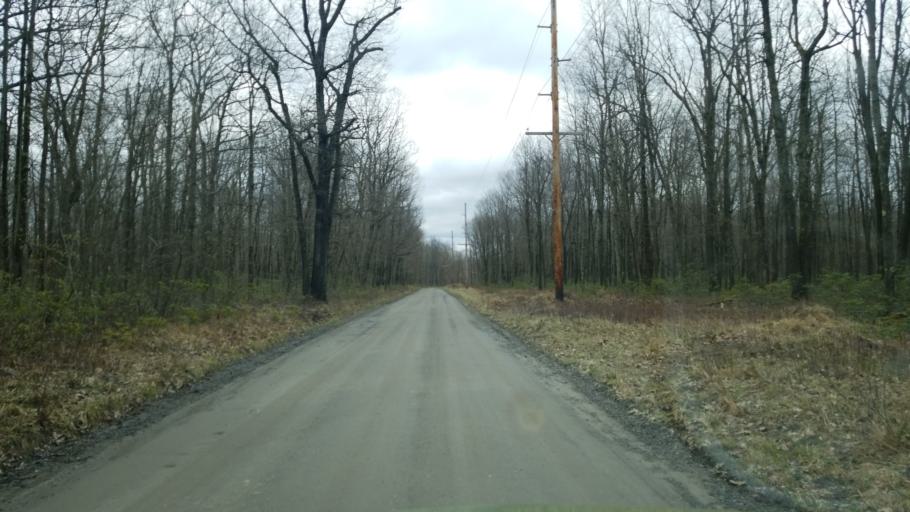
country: US
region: Pennsylvania
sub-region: Clearfield County
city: Shiloh
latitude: 41.1730
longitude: -78.2998
